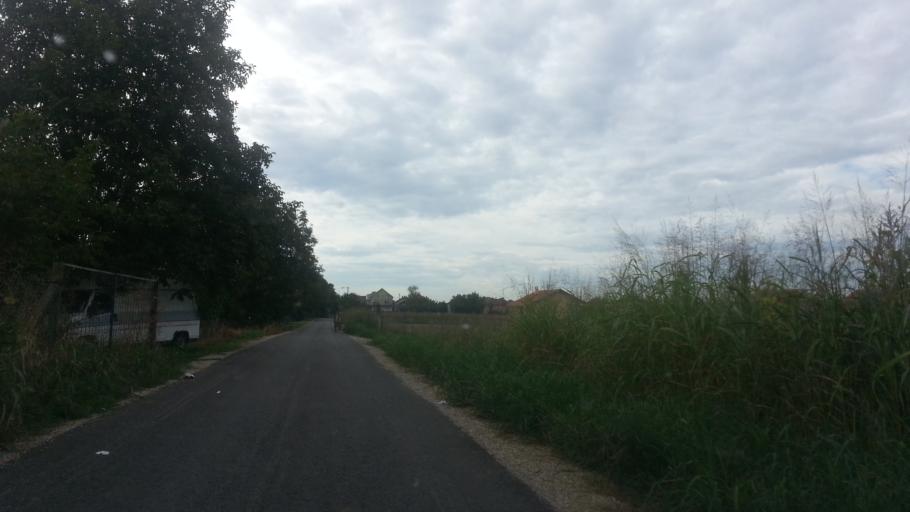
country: RS
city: Novi Banovci
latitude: 44.9622
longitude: 20.2729
